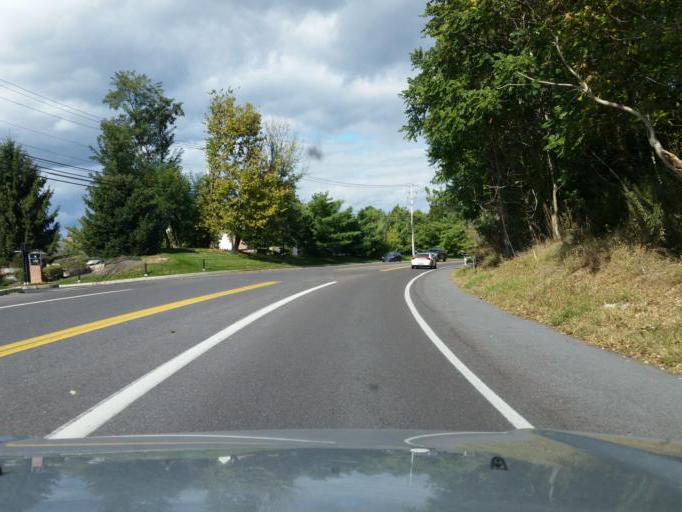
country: US
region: Pennsylvania
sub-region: Dauphin County
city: Hummelstown
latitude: 40.2491
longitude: -76.7082
